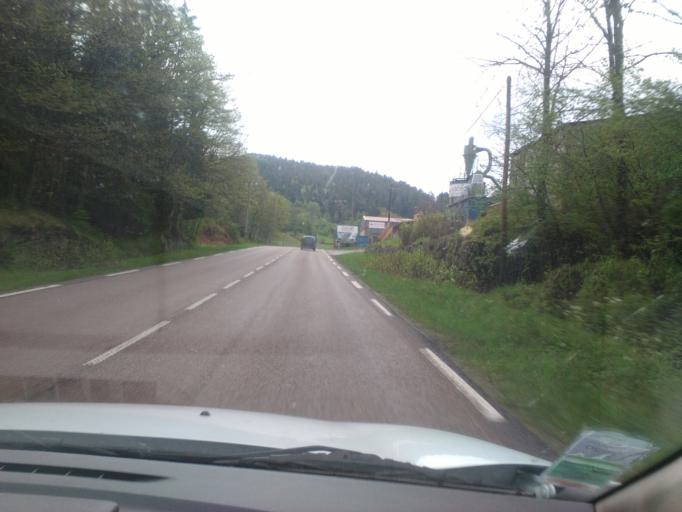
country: FR
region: Lorraine
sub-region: Departement des Vosges
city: Vagney
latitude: 47.9814
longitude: 6.7248
